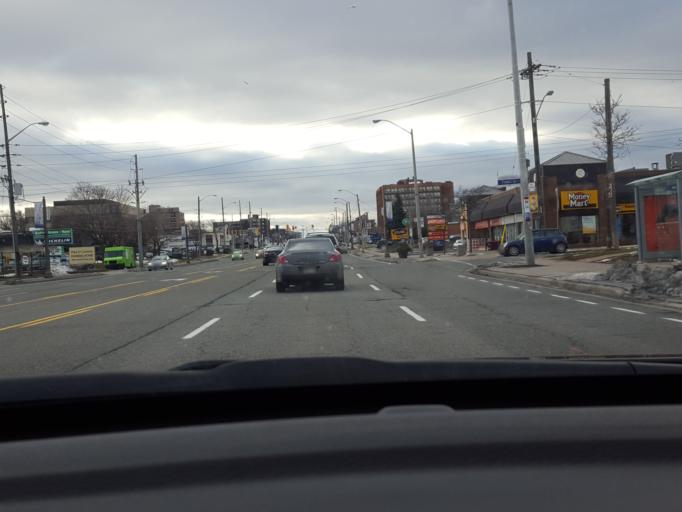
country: CA
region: Ontario
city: Scarborough
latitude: 43.7447
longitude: -79.2981
